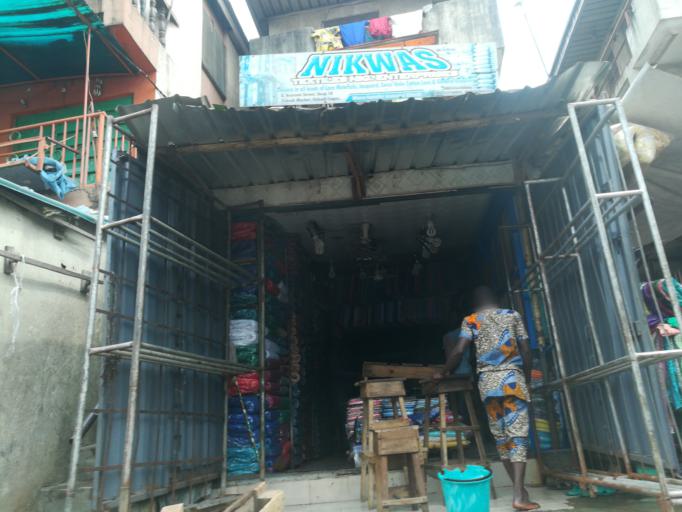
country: NG
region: Lagos
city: Oshodi
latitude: 6.5573
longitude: 3.3498
